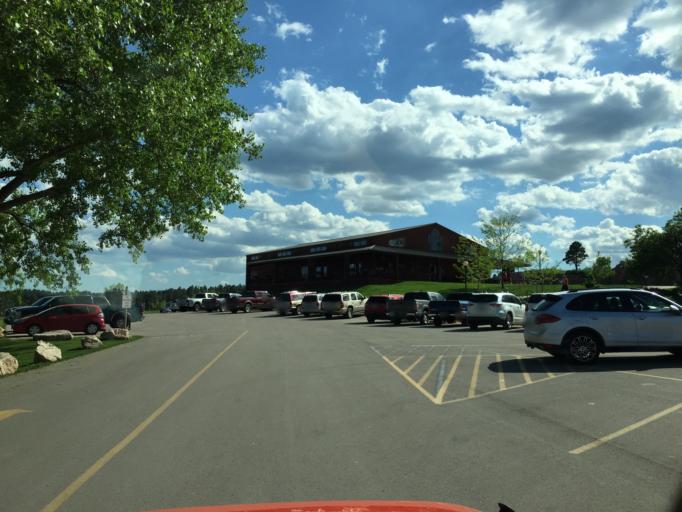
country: US
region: South Dakota
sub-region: Pennington County
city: Colonial Pine Hills
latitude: 43.9761
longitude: -103.3011
